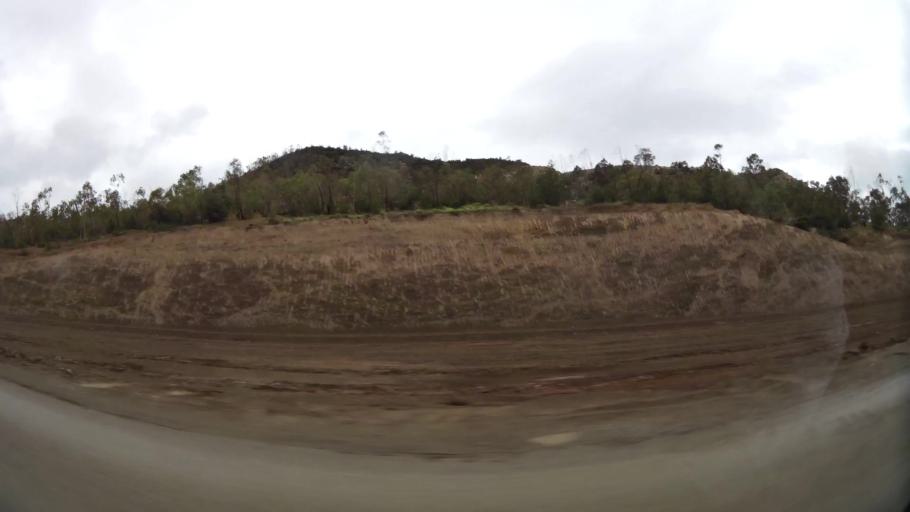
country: MA
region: Taza-Al Hoceima-Taounate
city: Imzourene
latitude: 34.9350
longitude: -3.8112
